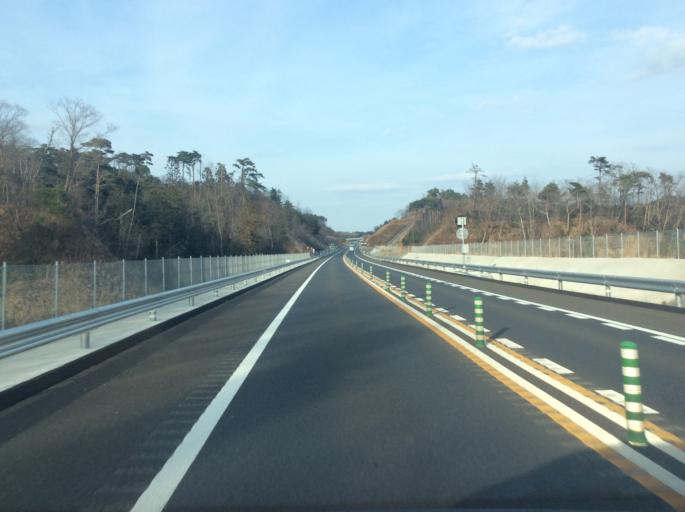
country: JP
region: Fukushima
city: Namie
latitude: 37.4464
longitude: 140.9587
